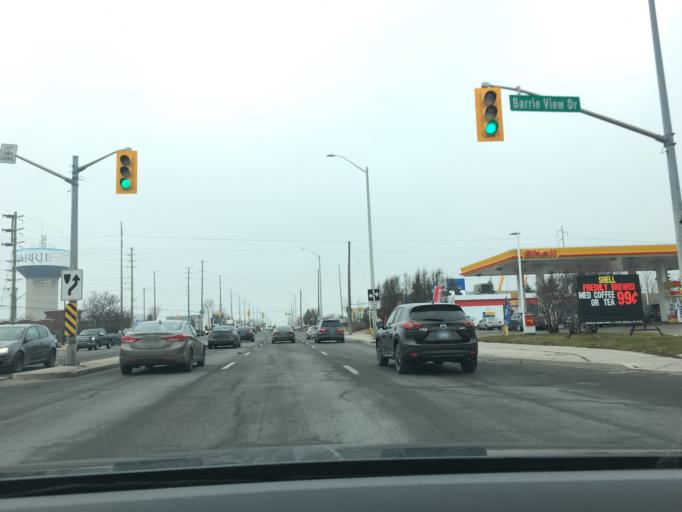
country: CA
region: Ontario
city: Innisfil
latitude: 44.3348
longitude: -79.6877
